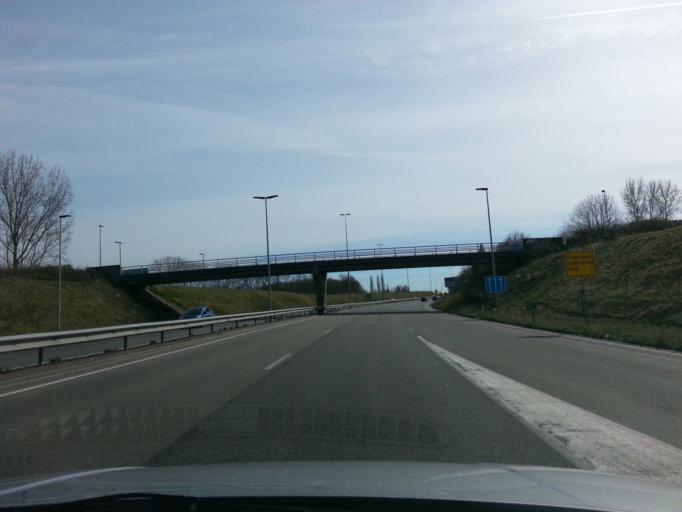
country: NL
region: Groningen
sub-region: Gemeente Groningen
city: Oosterpark
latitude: 53.2336
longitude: 6.6057
